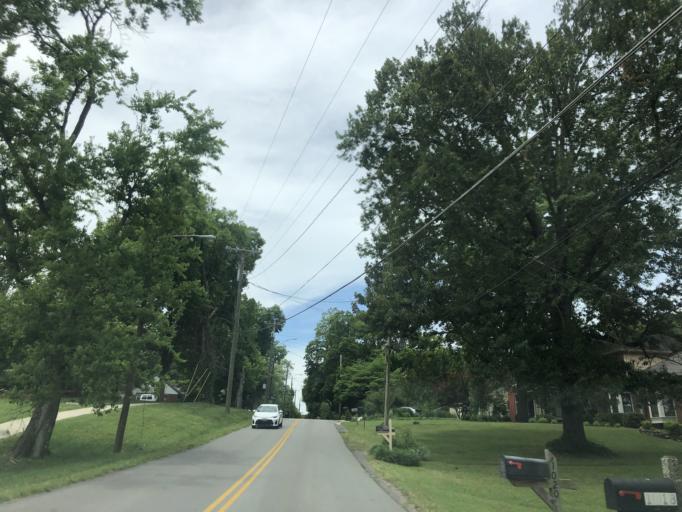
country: US
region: Tennessee
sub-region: Davidson County
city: Oak Hill
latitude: 36.1062
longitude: -86.7915
